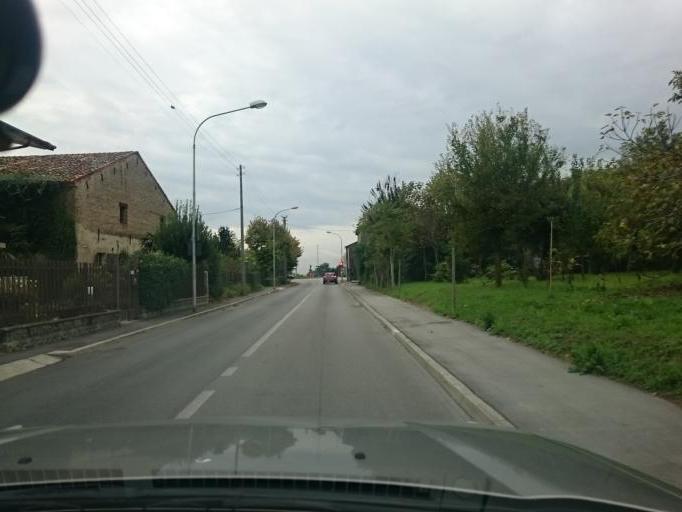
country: IT
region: Veneto
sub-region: Provincia di Padova
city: Vallonga
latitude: 45.2718
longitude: 12.0746
